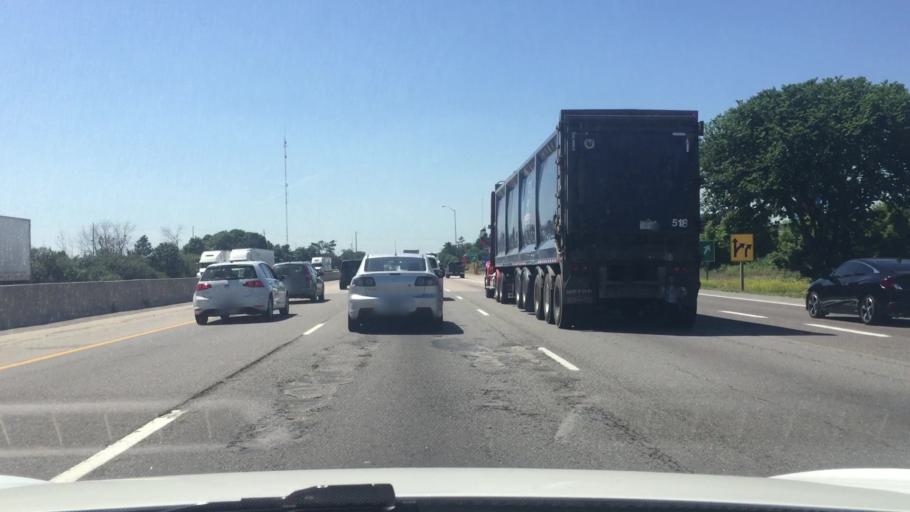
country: CA
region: Ontario
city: Oshawa
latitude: 43.8671
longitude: -78.9307
